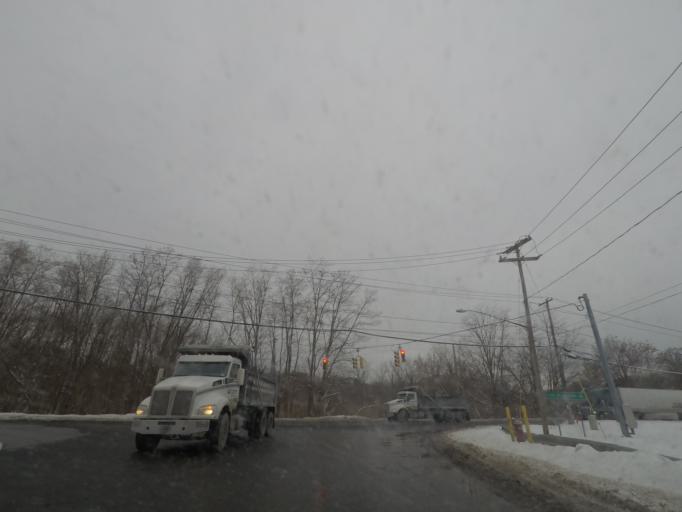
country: US
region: New York
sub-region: Rensselaer County
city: Rensselaer
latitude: 42.6213
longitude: -73.7668
